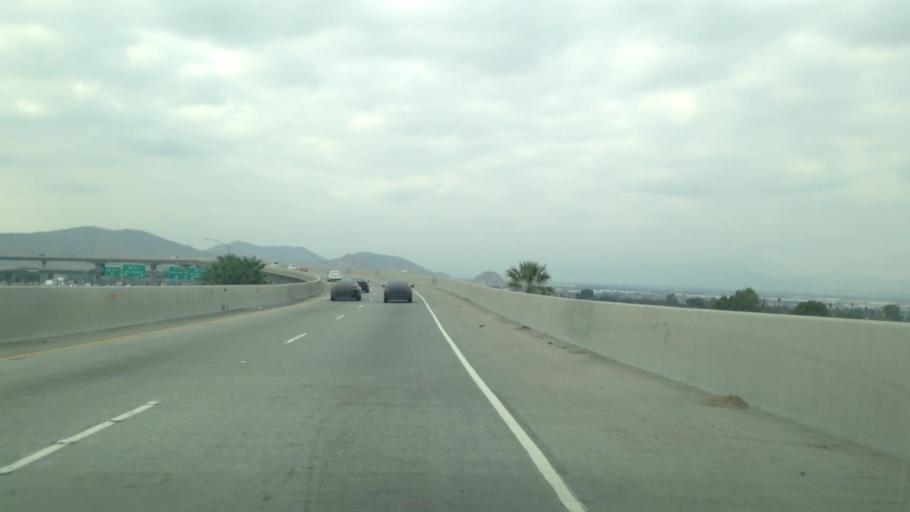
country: US
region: California
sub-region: Riverside County
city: Highgrove
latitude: 33.9895
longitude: -117.3491
